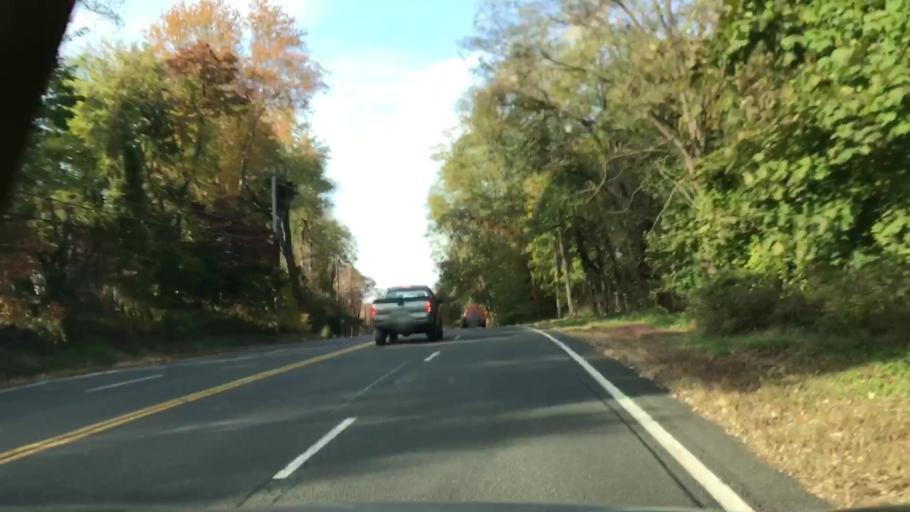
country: US
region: New York
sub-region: Rockland County
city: Tappan
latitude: 41.0273
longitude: -73.9433
